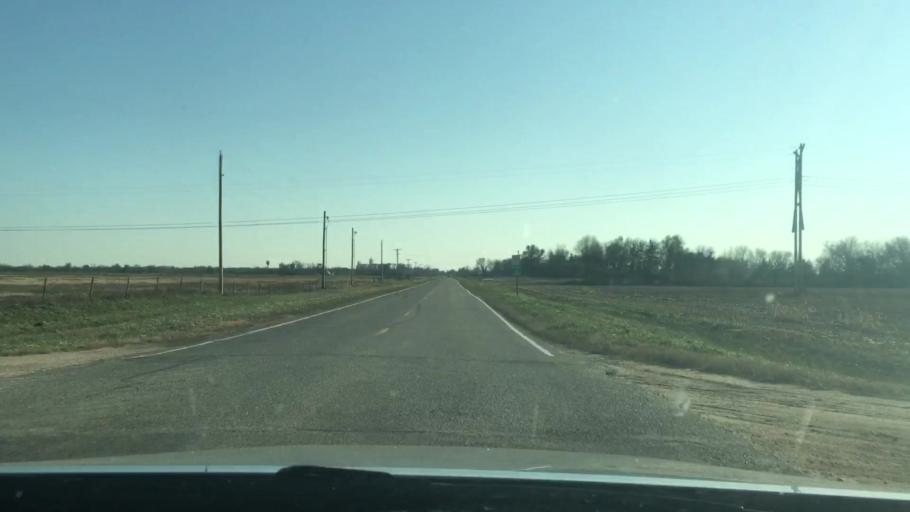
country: US
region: Kansas
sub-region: Reno County
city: Nickerson
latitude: 38.1736
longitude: -98.0876
